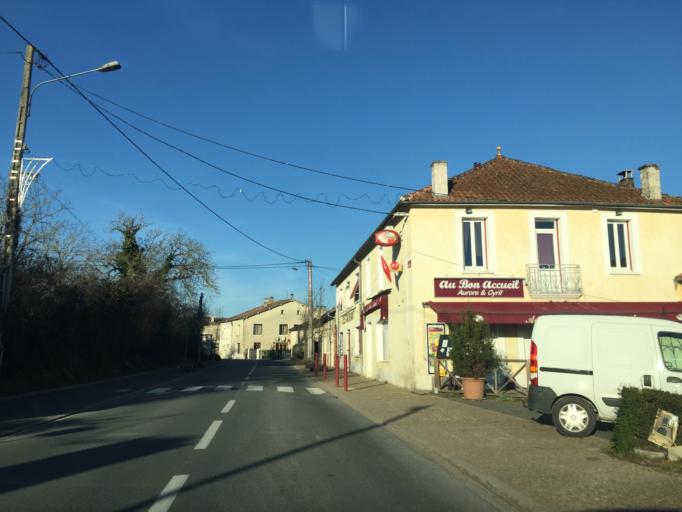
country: FR
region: Aquitaine
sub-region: Departement de la Dordogne
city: Neuvic
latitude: 45.1616
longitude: 0.3979
